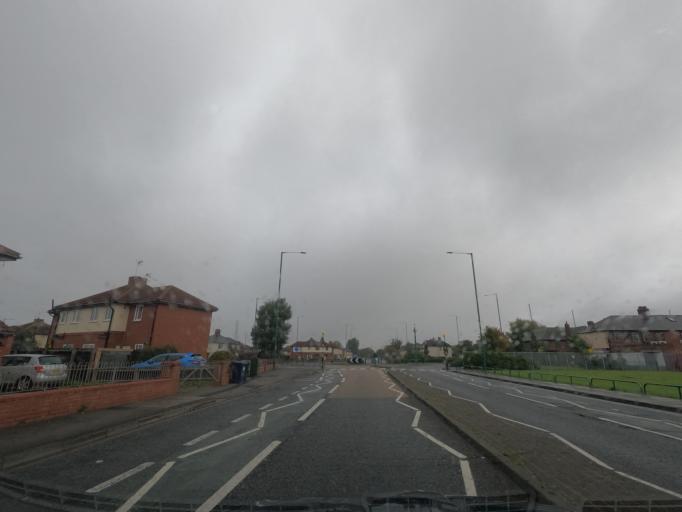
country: GB
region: England
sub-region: Redcar and Cleveland
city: South Bank
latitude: 54.5764
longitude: -1.1476
